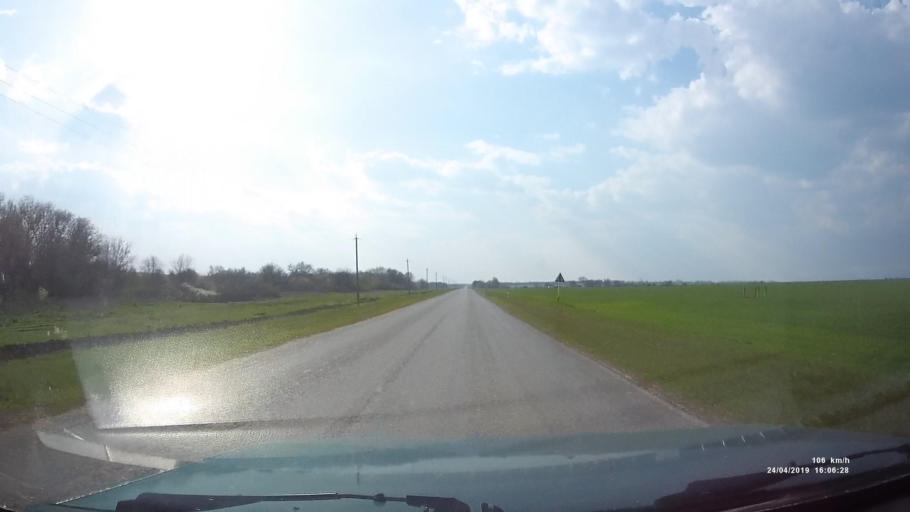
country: RU
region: Rostov
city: Sovetskoye
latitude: 46.6867
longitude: 42.3483
